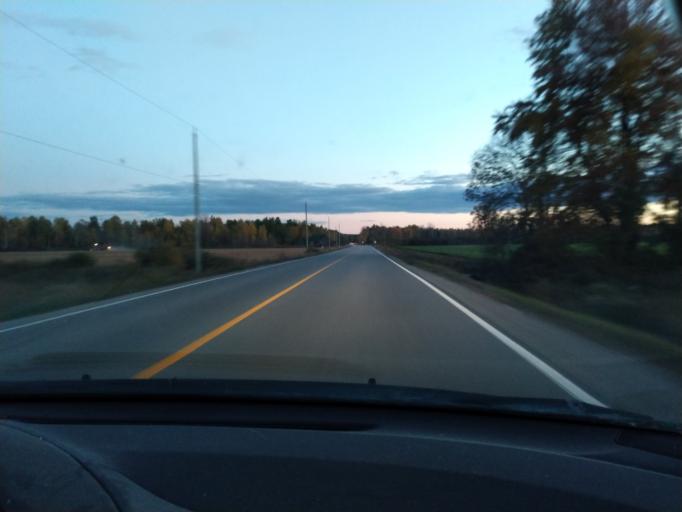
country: CA
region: Ontario
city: Bradford West Gwillimbury
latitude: 44.1927
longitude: -79.6629
